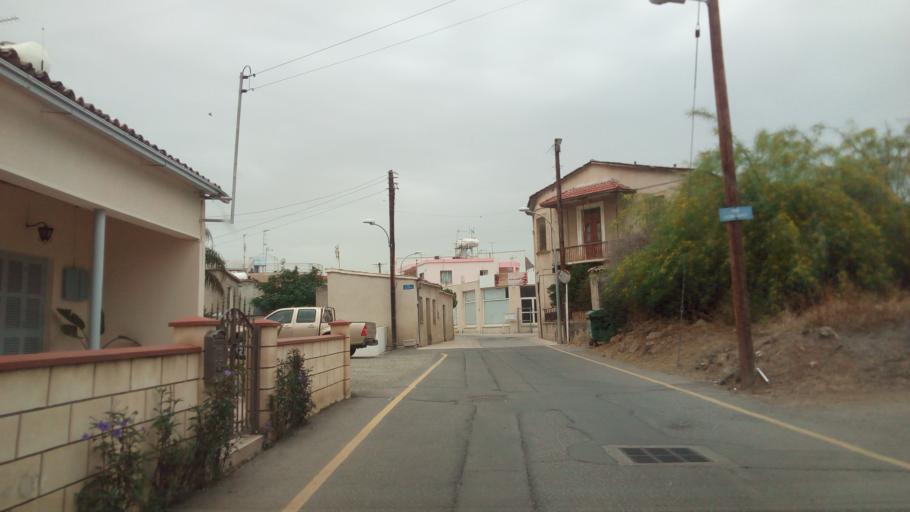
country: CY
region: Larnaka
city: Kornos
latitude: 34.9244
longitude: 33.3980
